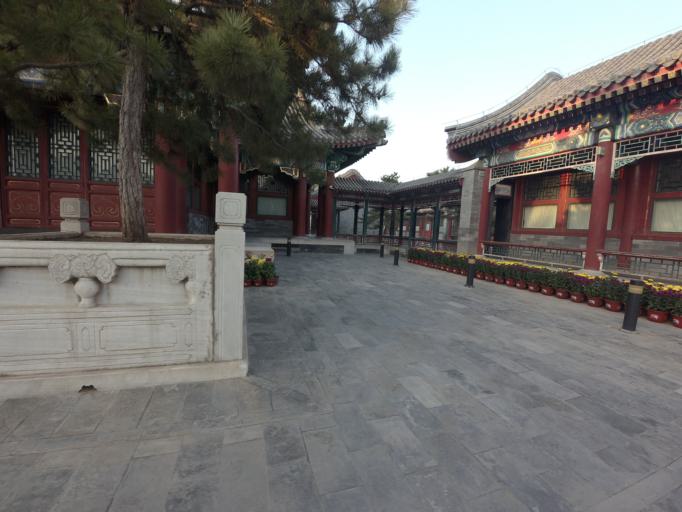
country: CN
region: Beijing
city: Haidian
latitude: 39.9957
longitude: 116.2749
